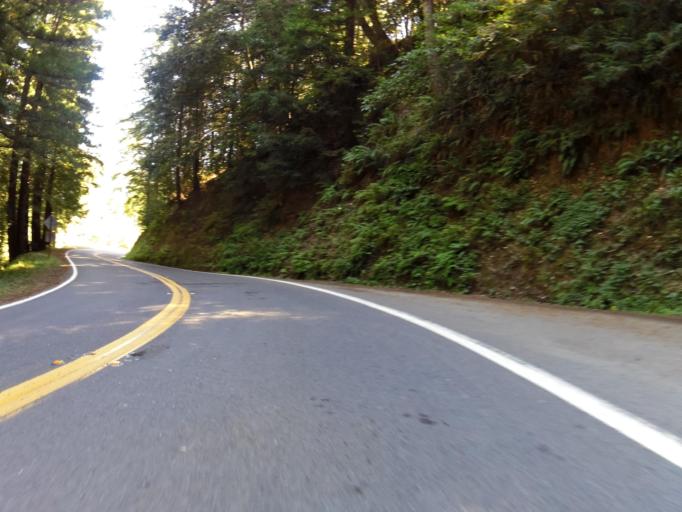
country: US
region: California
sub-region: Mendocino County
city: Fort Bragg
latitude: 39.7239
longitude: -123.8099
